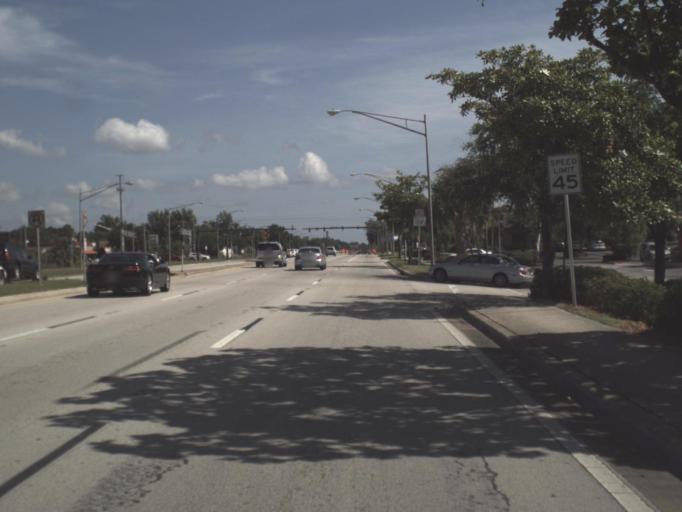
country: US
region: Florida
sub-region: Duval County
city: Jacksonville
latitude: 30.2803
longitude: -81.7201
